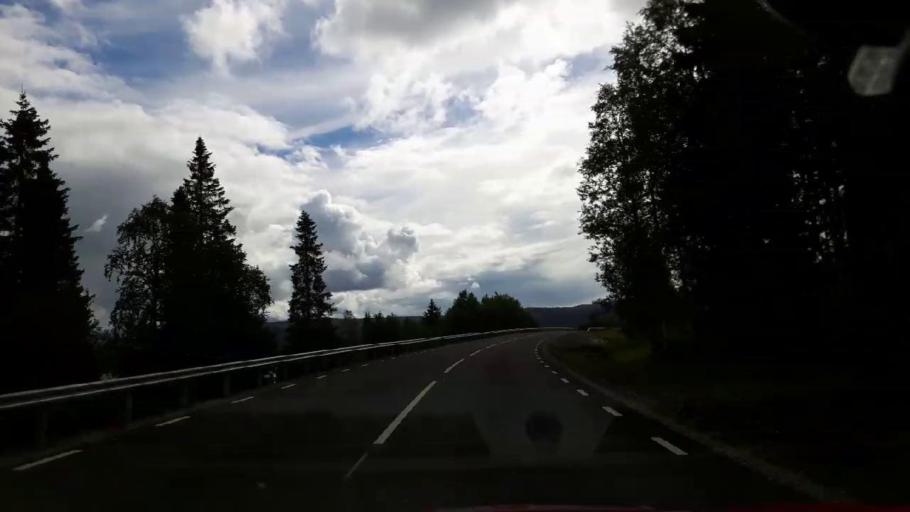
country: NO
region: Nord-Trondelag
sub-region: Royrvik
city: Royrvik
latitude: 64.8062
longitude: 14.0712
